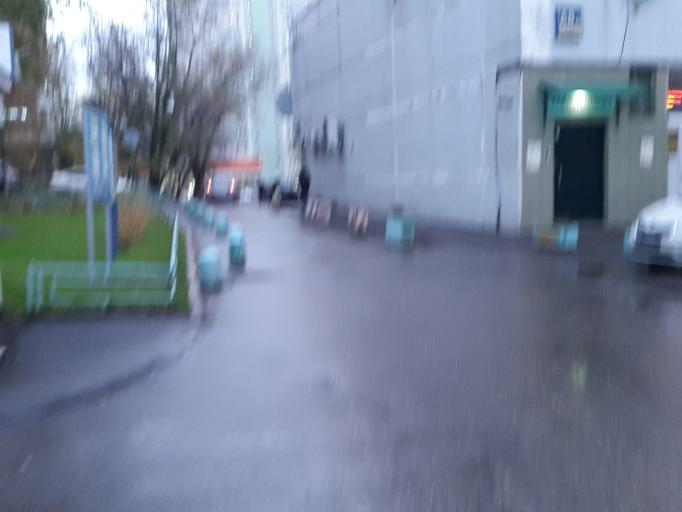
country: RU
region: Moscow
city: Pokrovskoye-Streshnevo
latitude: 55.8104
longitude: 37.4541
